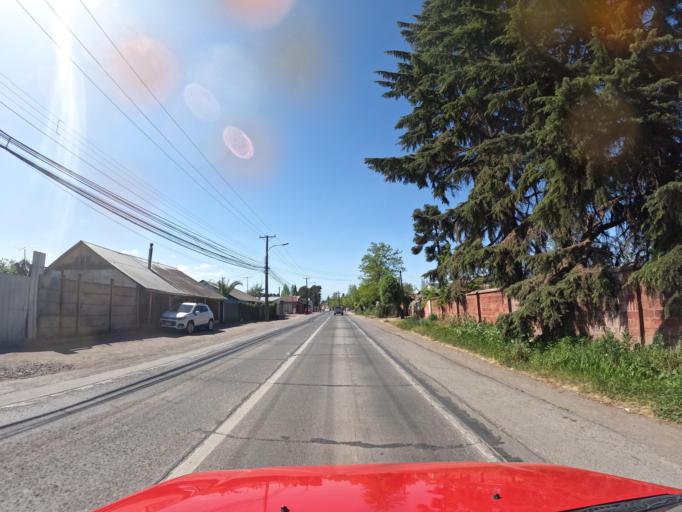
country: CL
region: Maule
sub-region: Provincia de Curico
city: Molina
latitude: -35.0746
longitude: -71.2574
